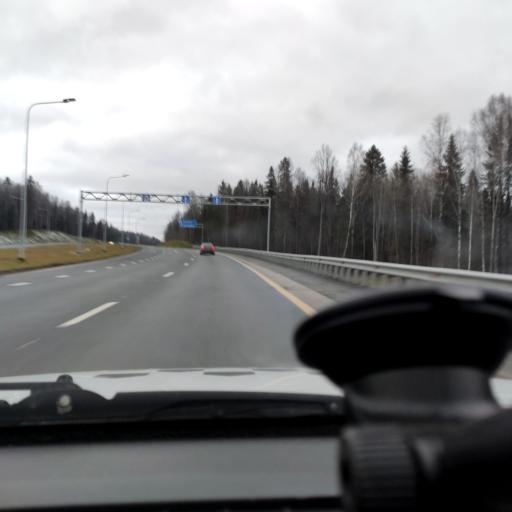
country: RU
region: Perm
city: Novyye Lyady
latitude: 58.0923
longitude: 56.4274
